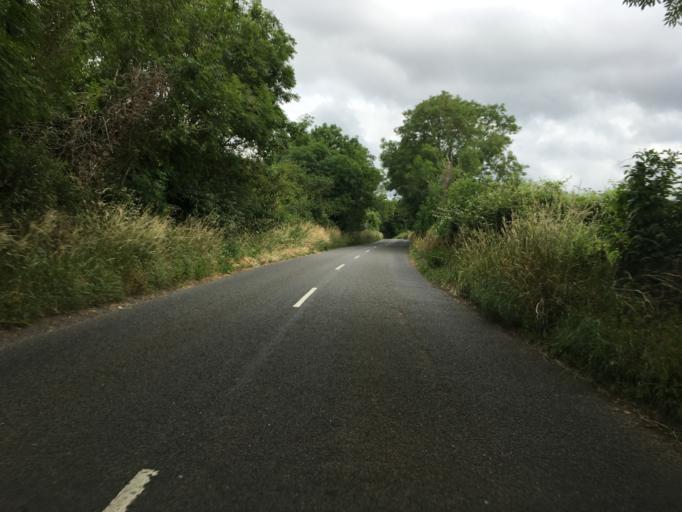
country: GB
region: England
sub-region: Oxfordshire
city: Charlbury
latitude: 51.8982
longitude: -1.4915
